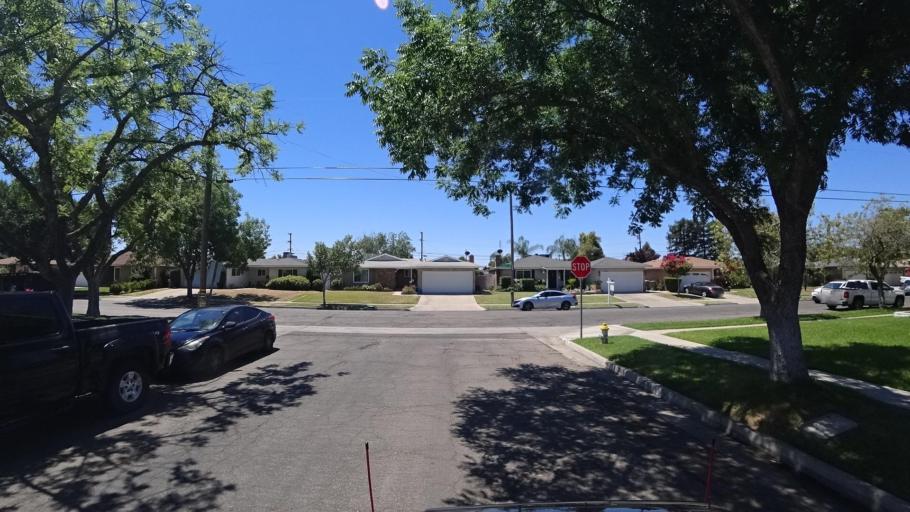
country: US
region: California
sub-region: Fresno County
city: Fresno
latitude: 36.8024
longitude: -119.7771
